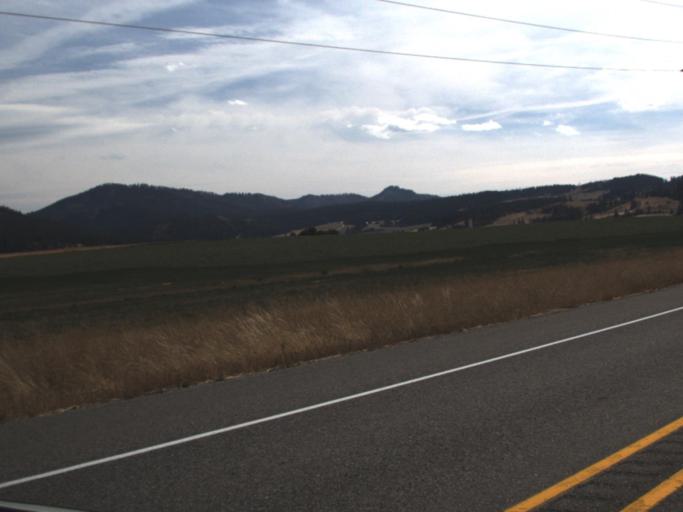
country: US
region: Washington
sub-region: Stevens County
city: Chewelah
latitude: 48.2347
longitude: -117.7153
